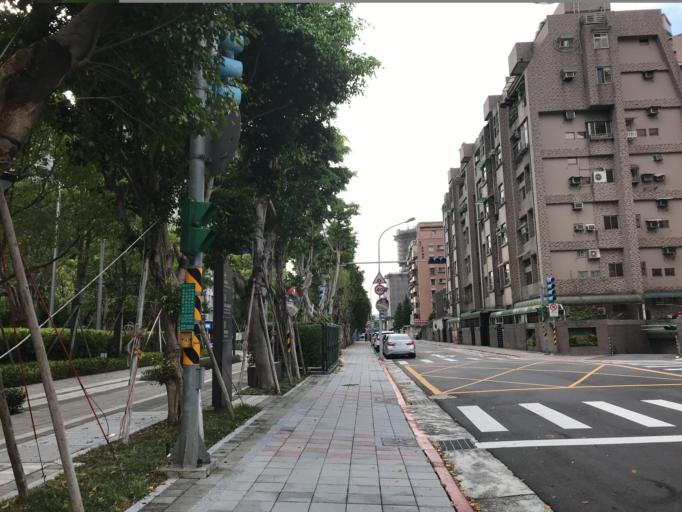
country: TW
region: Taipei
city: Taipei
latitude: 24.9966
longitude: 121.5399
